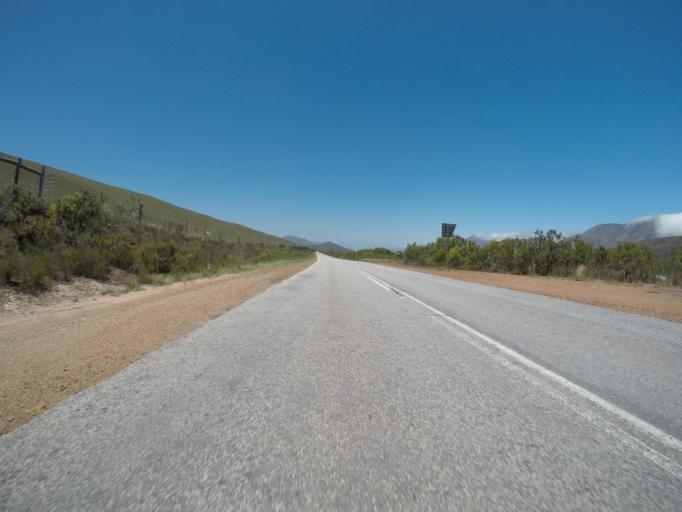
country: ZA
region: Eastern Cape
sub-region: Cacadu District Municipality
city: Kareedouw
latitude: -33.8480
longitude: 23.9599
